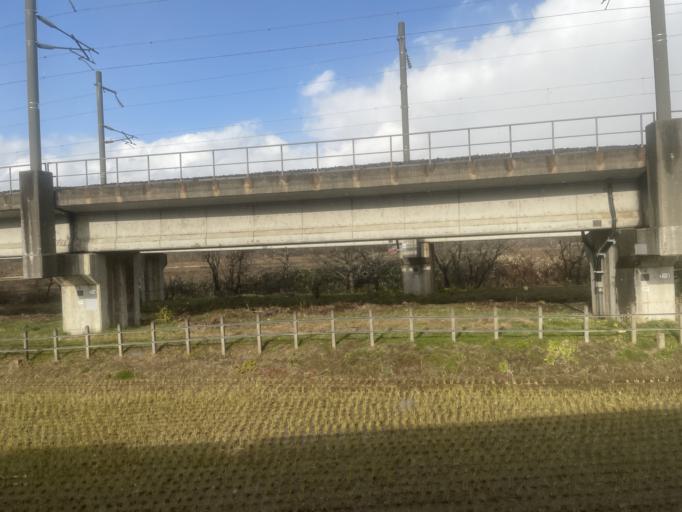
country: JP
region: Aomori
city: Goshogawara
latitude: 41.0658
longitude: 140.5644
